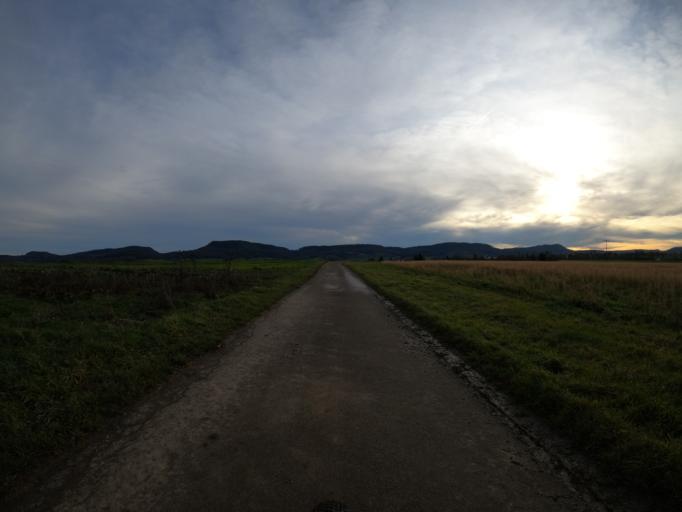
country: DE
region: Baden-Wuerttemberg
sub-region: Regierungsbezirk Stuttgart
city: Heiningen
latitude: 48.6723
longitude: 9.6498
